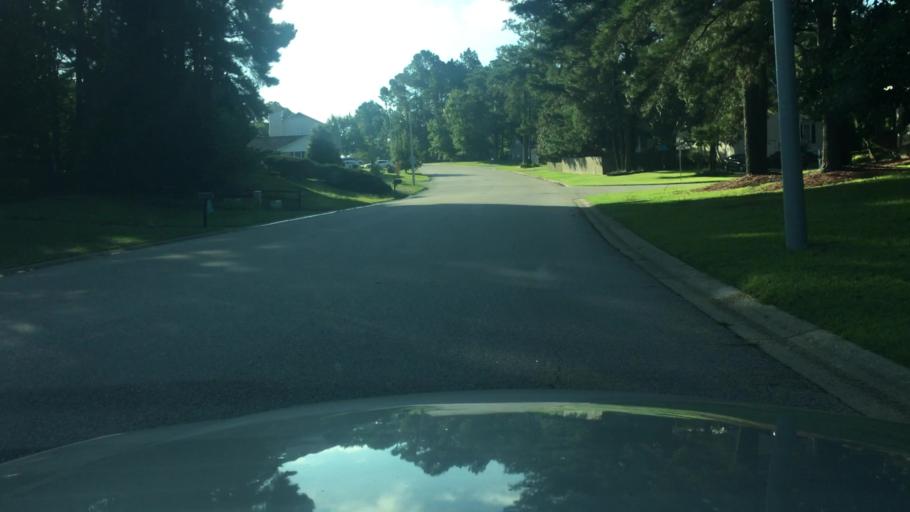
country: US
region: North Carolina
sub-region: Cumberland County
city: Fayetteville
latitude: 35.1415
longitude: -78.8801
